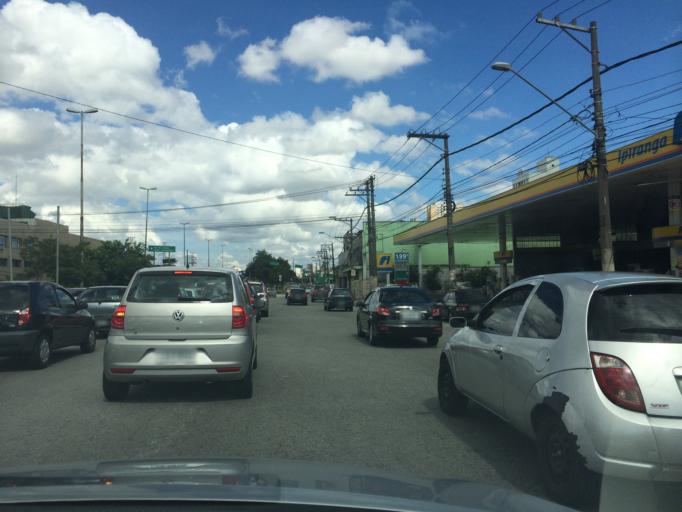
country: BR
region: Sao Paulo
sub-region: Guarulhos
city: Guarulhos
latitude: -23.5250
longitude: -46.5572
